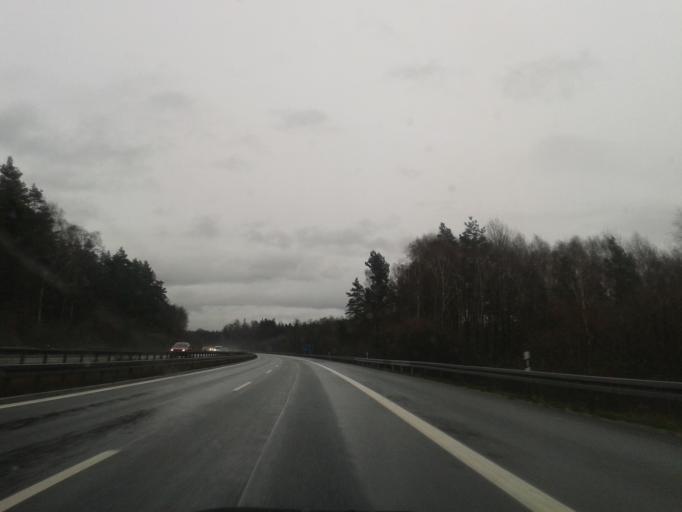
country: DE
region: Saxony
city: Lichtenberg
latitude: 51.1553
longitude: 13.9828
